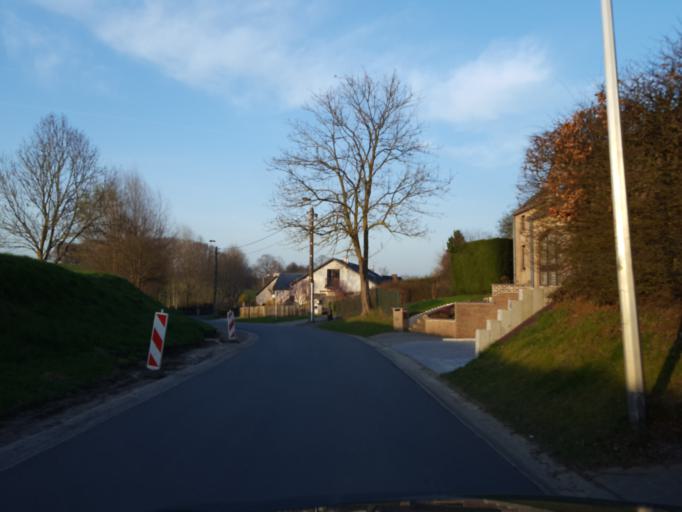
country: BE
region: Wallonia
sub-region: Province du Brabant Wallon
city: Louvain-la-Neuve
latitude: 50.6755
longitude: 4.6351
